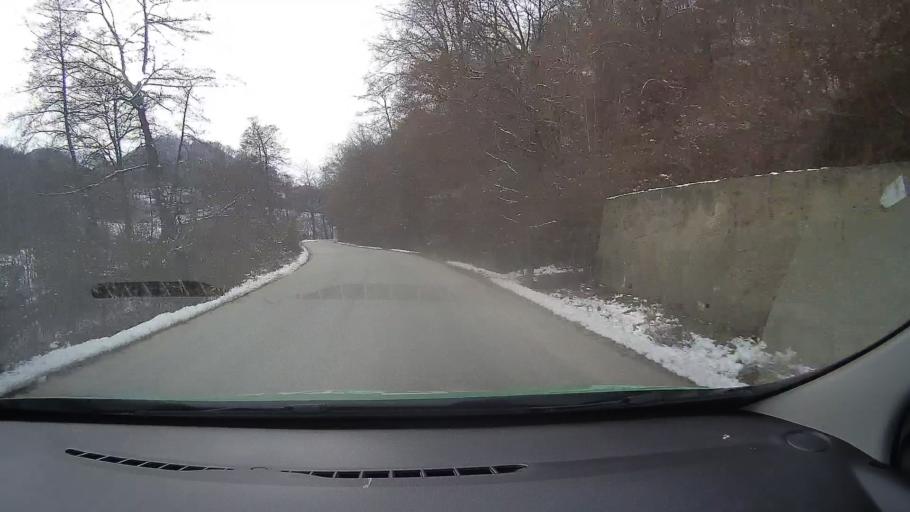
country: RO
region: Alba
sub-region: Oras Zlatna
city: Zlatna
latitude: 46.1110
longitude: 23.1987
